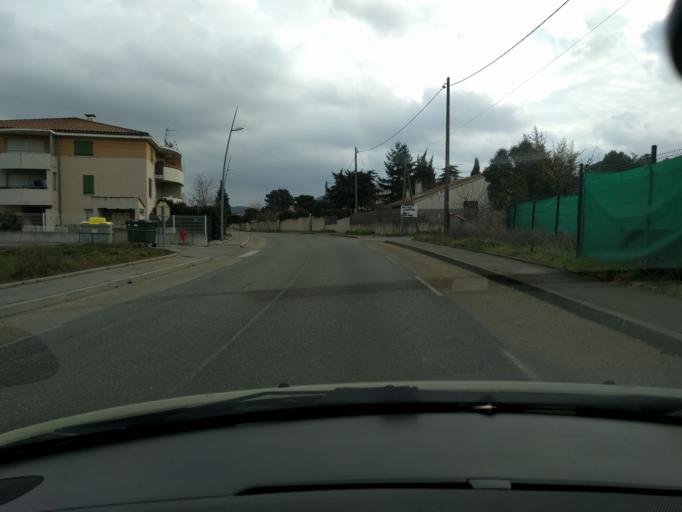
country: FR
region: Provence-Alpes-Cote d'Azur
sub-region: Departement des Bouches-du-Rhone
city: Simiane-Collongue
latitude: 43.4360
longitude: 5.4201
